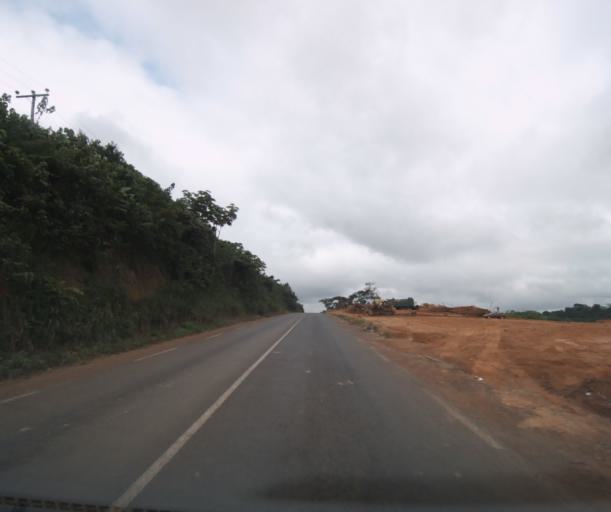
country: CM
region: Centre
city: Mbankomo
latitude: 3.7844
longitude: 11.4629
